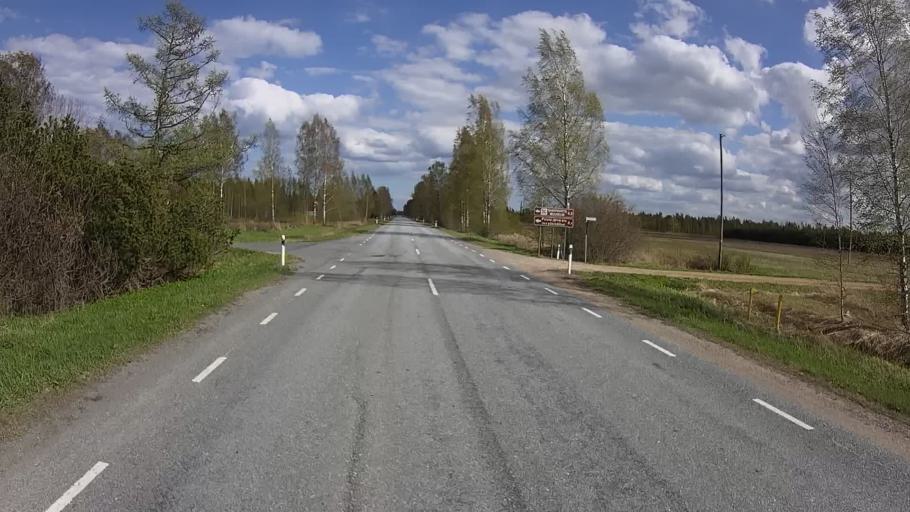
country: EE
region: Jogevamaa
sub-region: Mustvee linn
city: Mustvee
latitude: 58.7916
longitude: 26.9500
